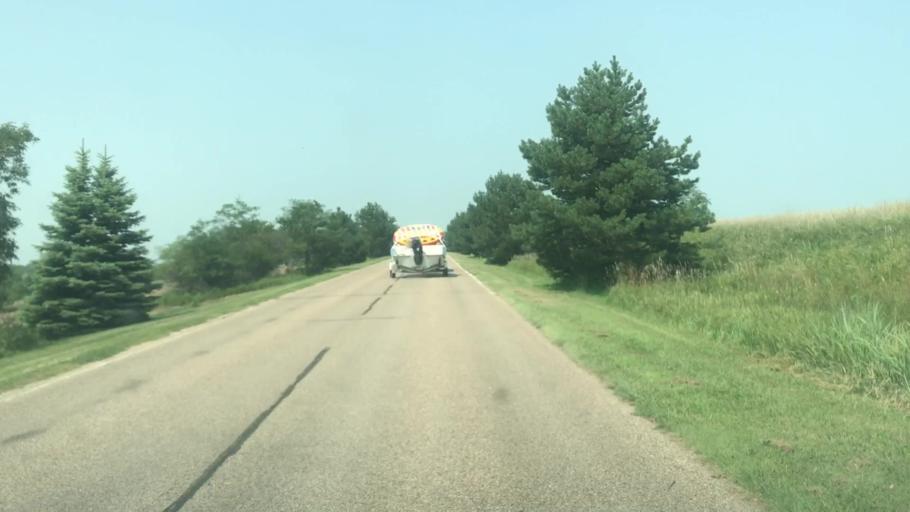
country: US
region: Nebraska
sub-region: Sherman County
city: Loup City
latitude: 41.2886
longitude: -98.8933
